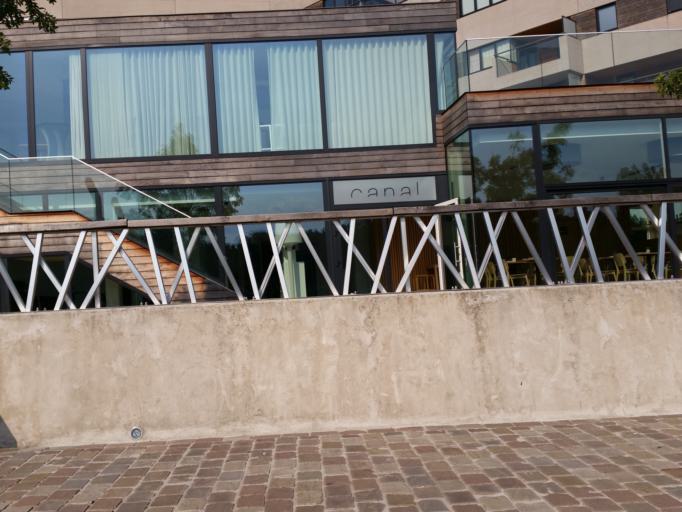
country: BE
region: Flanders
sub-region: Provincie Vlaams-Brabant
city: Vilvoorde
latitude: 50.9241
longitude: 4.4198
